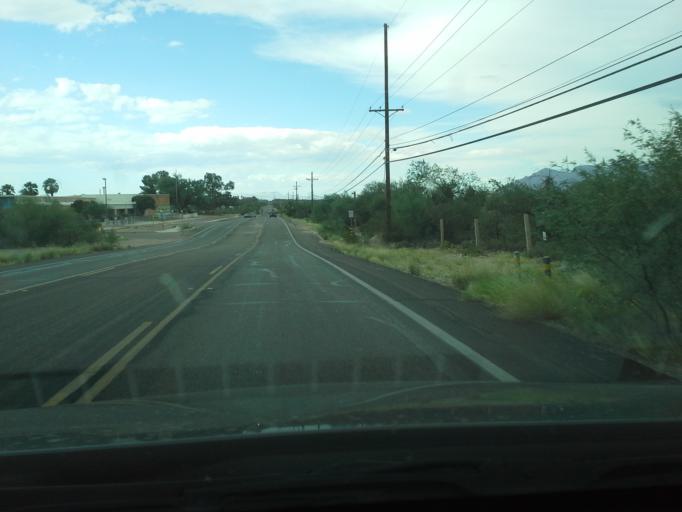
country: US
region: Arizona
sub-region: Pima County
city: South Tucson
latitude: 32.2087
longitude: -111.0203
